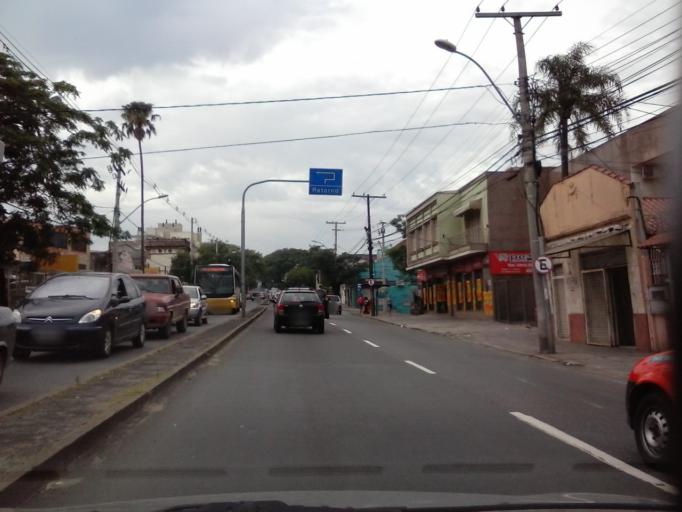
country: BR
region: Rio Grande do Sul
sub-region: Porto Alegre
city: Porto Alegre
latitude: -30.0693
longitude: -51.2050
